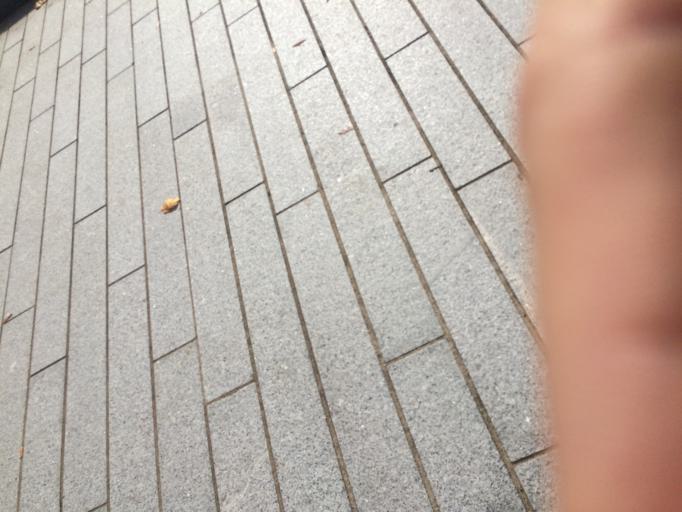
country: GB
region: Scotland
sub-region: Edinburgh
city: Edinburgh
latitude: 55.9227
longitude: -3.1753
